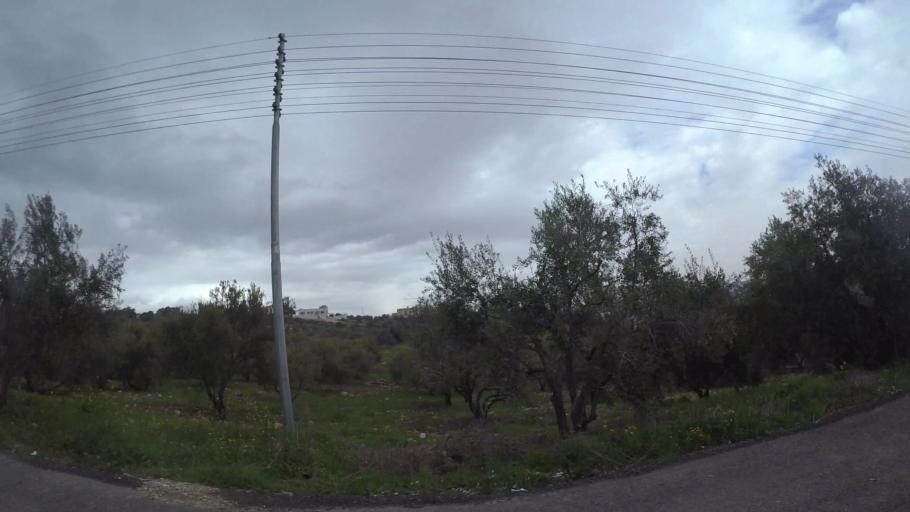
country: JO
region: Amman
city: Umm as Summaq
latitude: 31.9109
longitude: 35.8404
